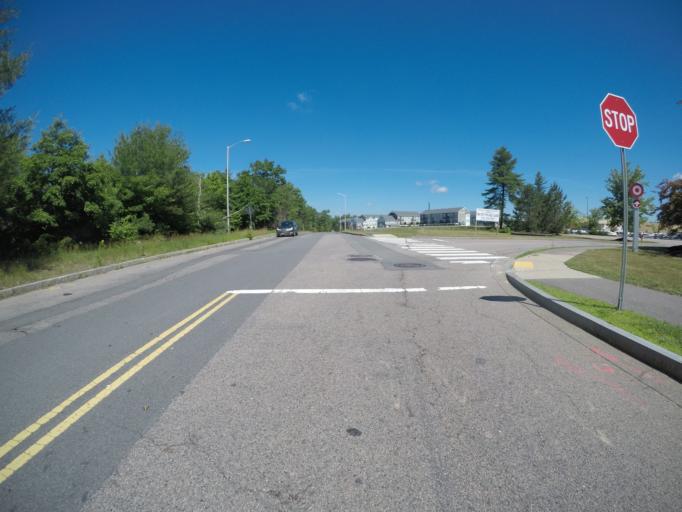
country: US
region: Massachusetts
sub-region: Bristol County
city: Easton
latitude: 42.0253
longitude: -71.1440
